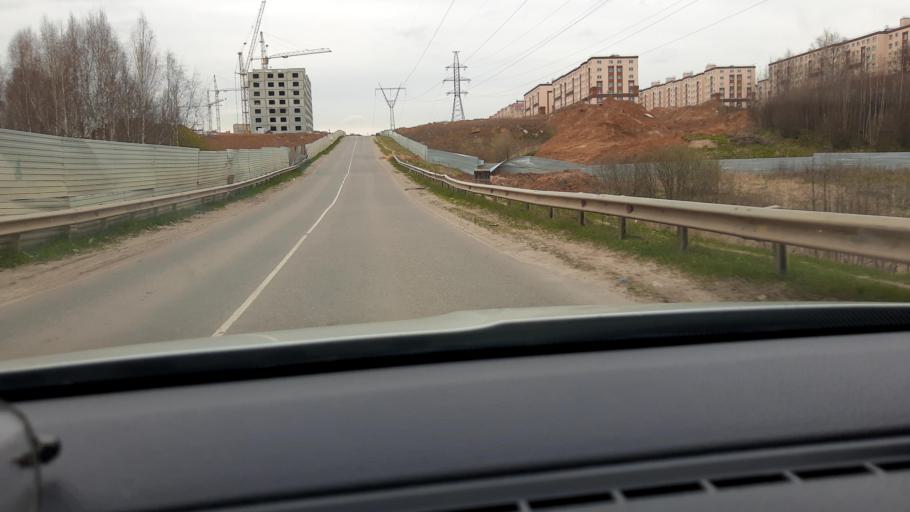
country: RU
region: Moscow
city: Zagor'ye
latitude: 55.5275
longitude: 37.6380
